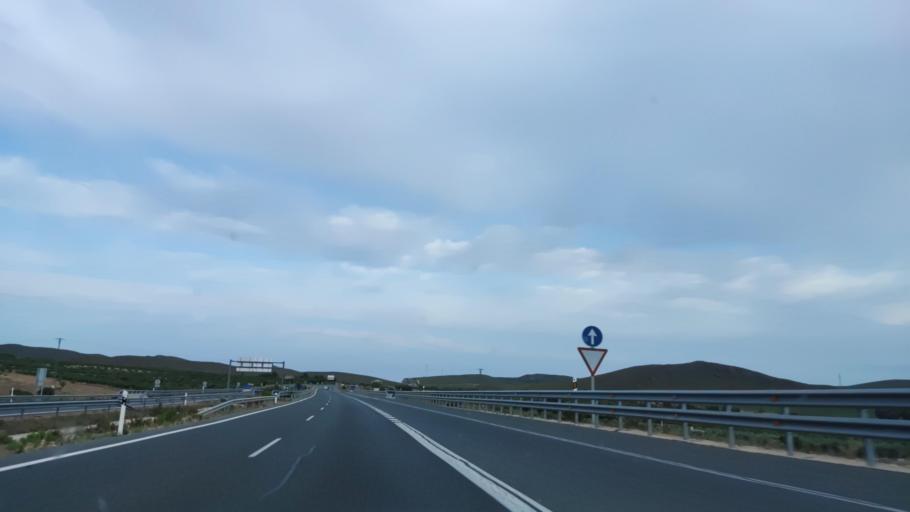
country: ES
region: Castille-La Mancha
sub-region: Provincia de Albacete
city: Hellin
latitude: 38.5378
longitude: -1.6897
